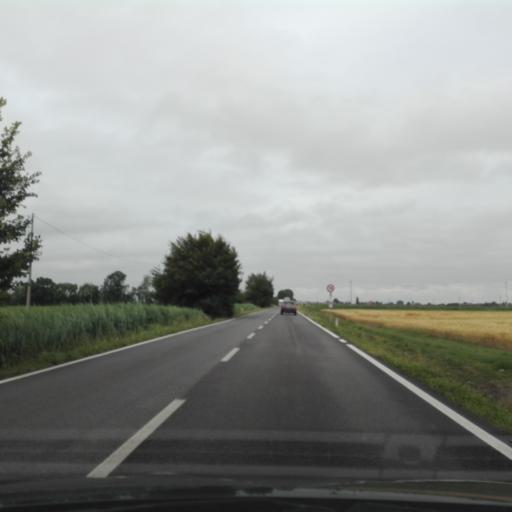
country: IT
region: Veneto
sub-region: Provincia di Rovigo
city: Costa di Rovigo
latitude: 45.0771
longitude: 11.6975
